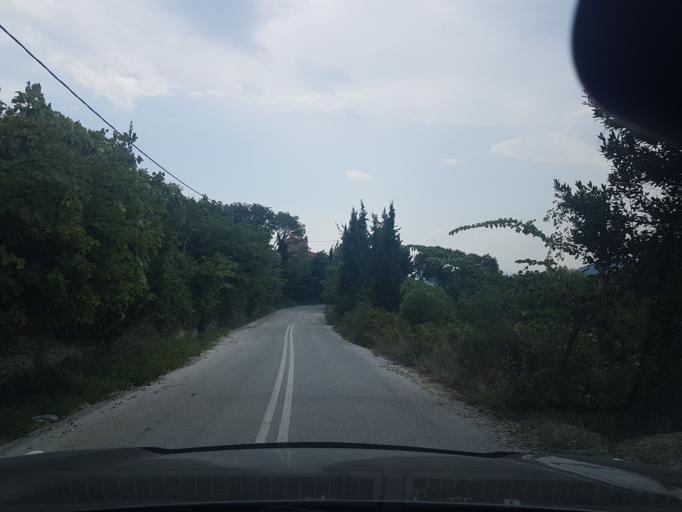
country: GR
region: Central Greece
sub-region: Nomos Evvoias
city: Kymi
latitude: 38.6403
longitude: 24.0665
